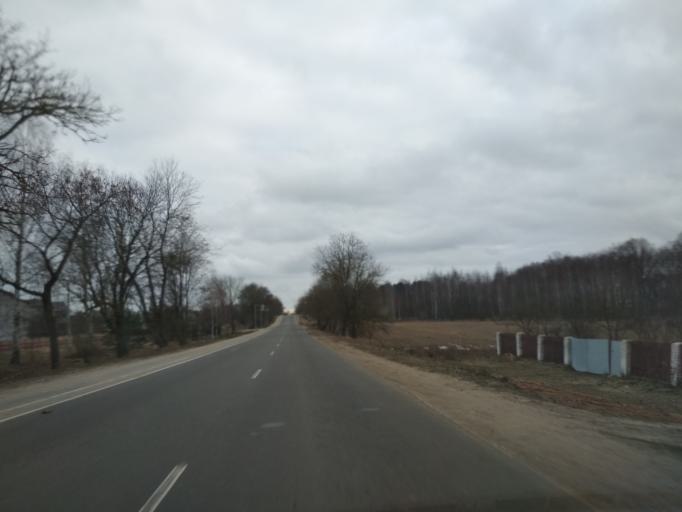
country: BY
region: Minsk
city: Druzhny
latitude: 53.5719
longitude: 27.9499
